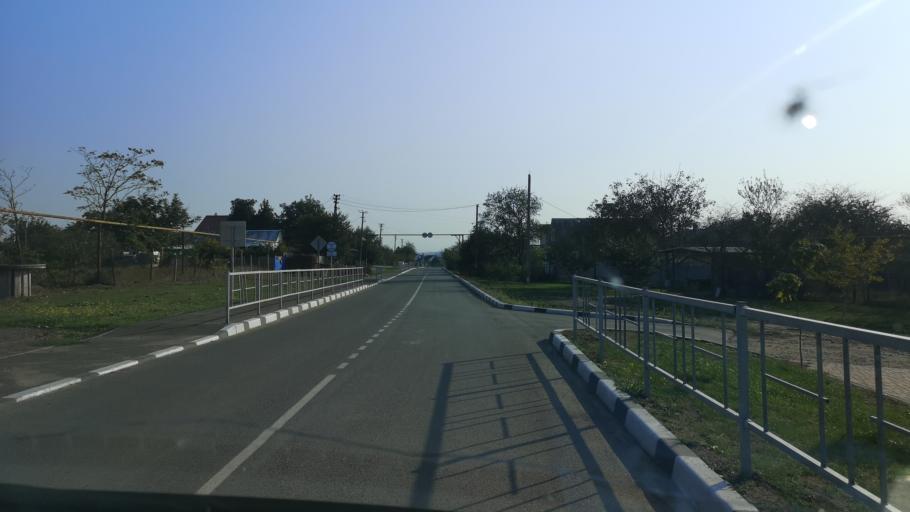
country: RU
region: Krasnodarskiy
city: Taman'
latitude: 45.2136
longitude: 36.6986
